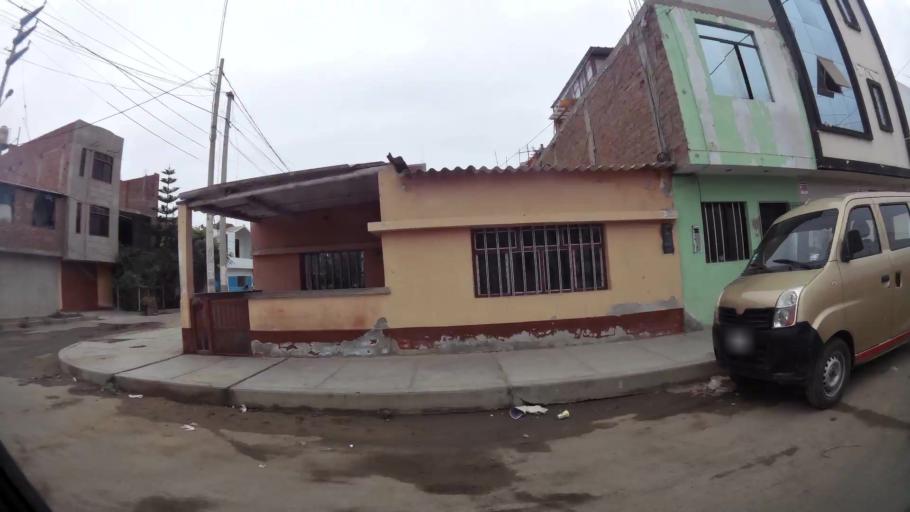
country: PE
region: La Libertad
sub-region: Provincia de Trujillo
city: Buenos Aires
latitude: -8.1413
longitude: -79.0465
